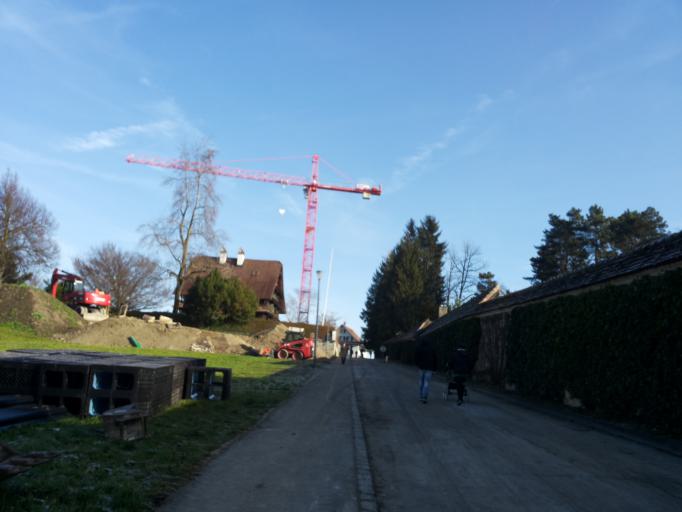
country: CH
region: Zug
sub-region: Zug
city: Cham
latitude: 47.1795
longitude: 8.4645
